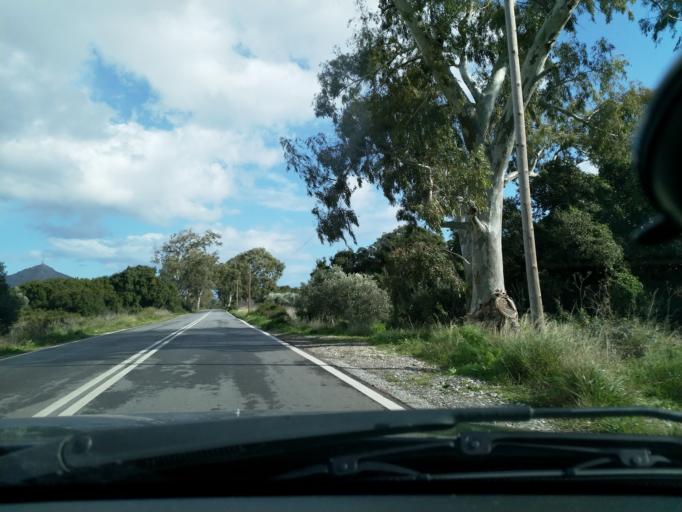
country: GR
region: Crete
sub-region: Nomos Chanias
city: Mouzouras
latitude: 35.5181
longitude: 24.1375
